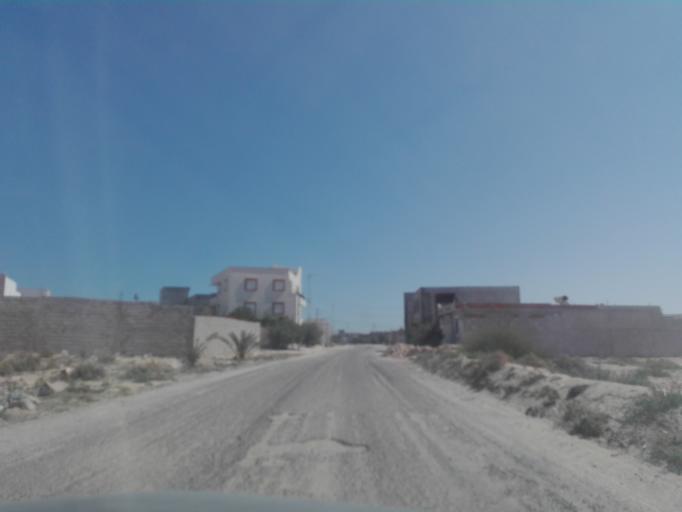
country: TN
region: Qabis
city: Gabes
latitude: 33.8702
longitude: 10.0473
